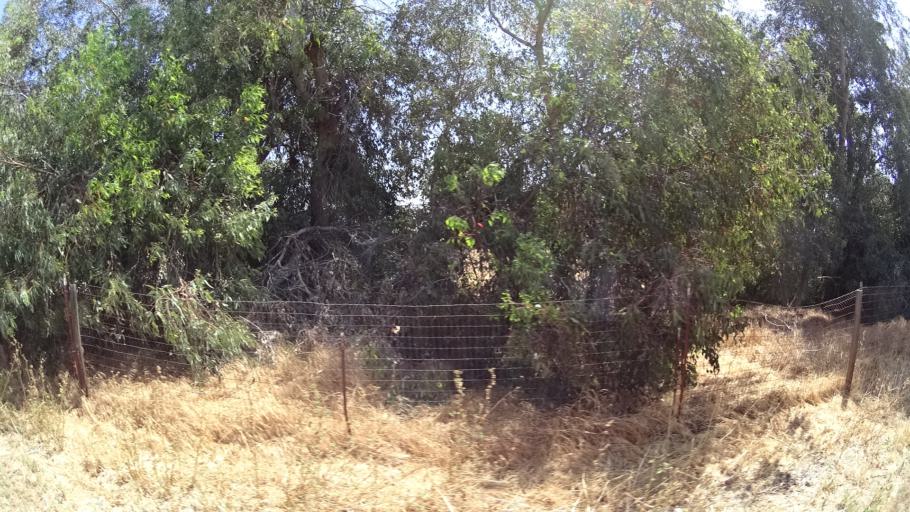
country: US
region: California
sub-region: Kings County
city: Armona
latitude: 36.2850
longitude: -119.6906
